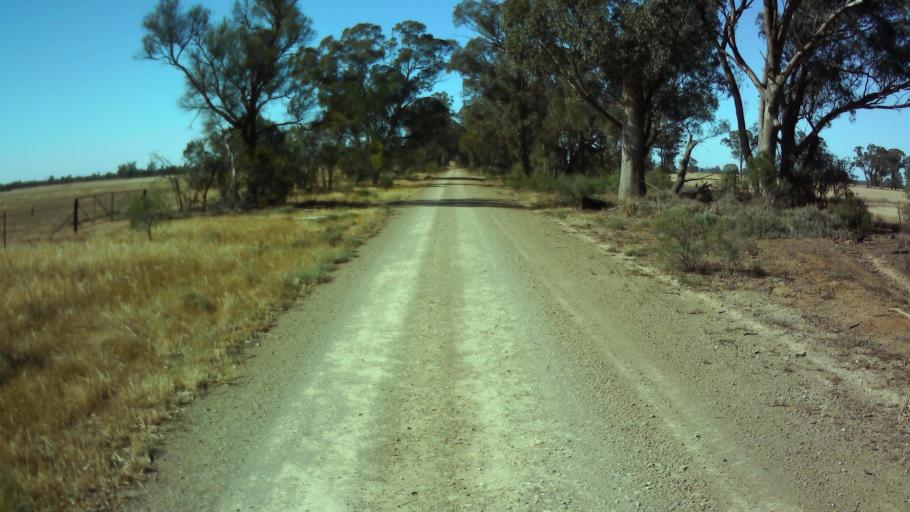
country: AU
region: New South Wales
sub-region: Weddin
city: Grenfell
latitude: -33.9183
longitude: 147.8753
